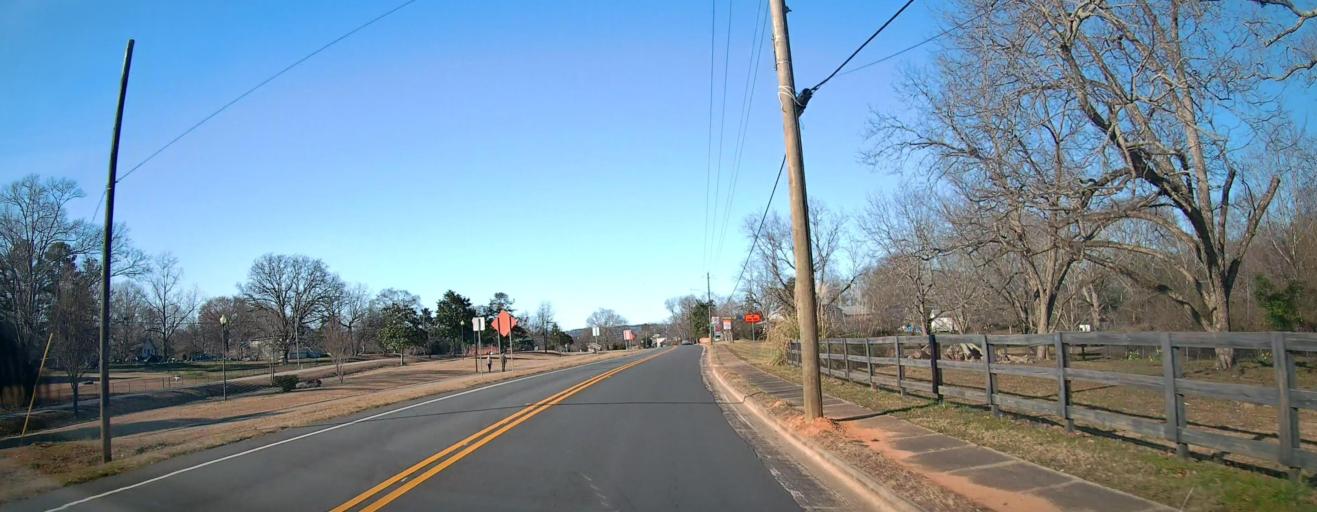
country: US
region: Georgia
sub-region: Talbot County
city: Sardis
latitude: 32.8056
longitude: -84.6958
